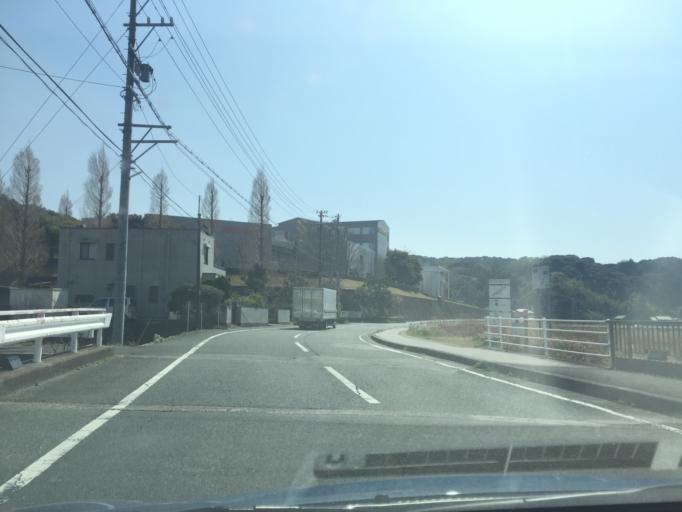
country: JP
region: Shizuoka
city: Hamamatsu
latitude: 34.7861
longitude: 137.6435
